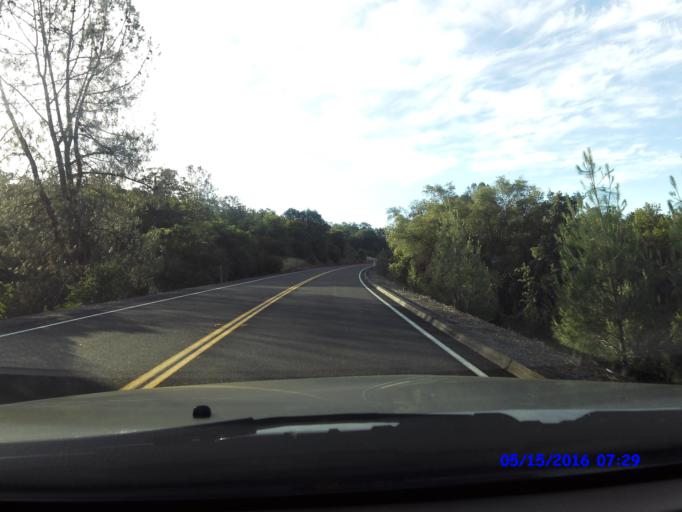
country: US
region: California
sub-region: Tuolumne County
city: Tuolumne City
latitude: 37.7324
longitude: -120.2143
